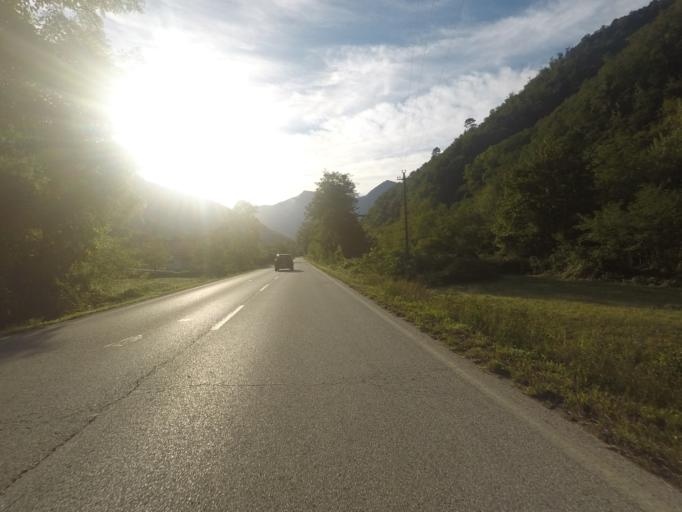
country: IT
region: Tuscany
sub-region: Provincia di Lucca
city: Valdottavo
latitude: 43.9694
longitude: 10.4907
